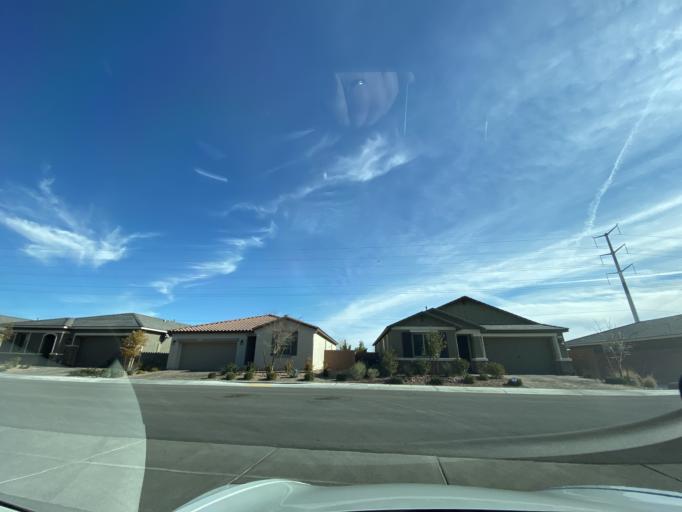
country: US
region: Nevada
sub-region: Clark County
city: Summerlin South
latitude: 36.2904
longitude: -115.3296
